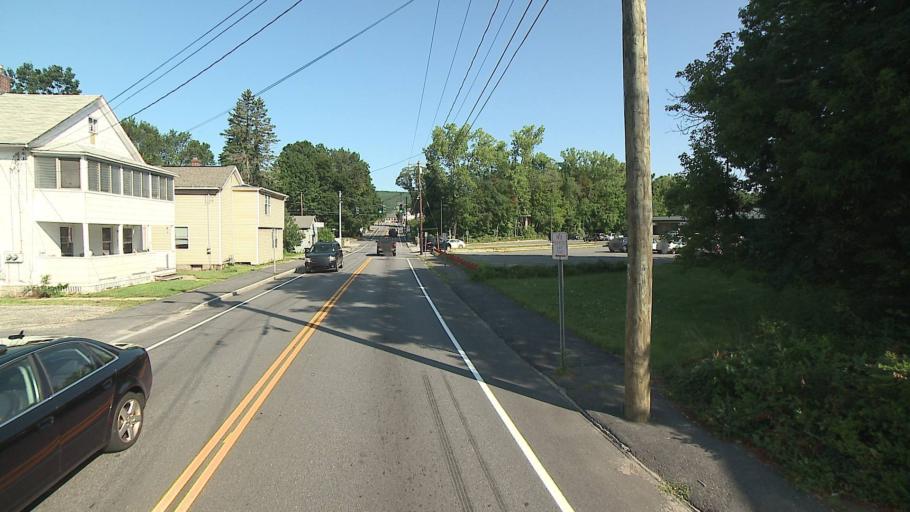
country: US
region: Connecticut
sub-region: Litchfield County
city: Torrington
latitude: 41.8090
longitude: -73.1174
